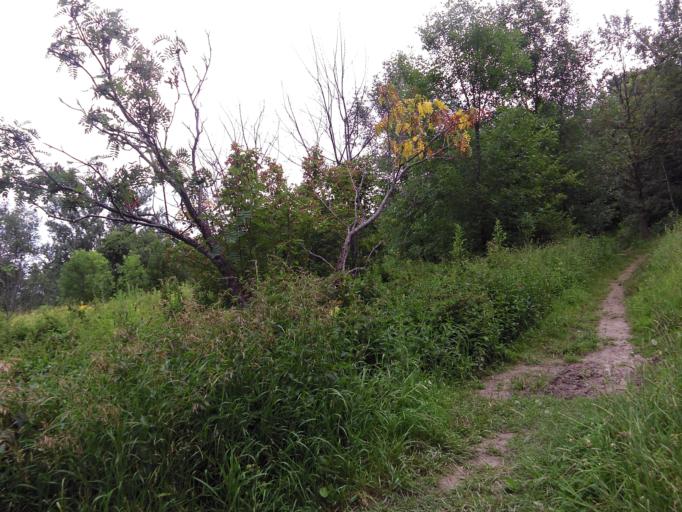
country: CA
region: Ontario
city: Ottawa
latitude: 45.3863
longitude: -75.7026
